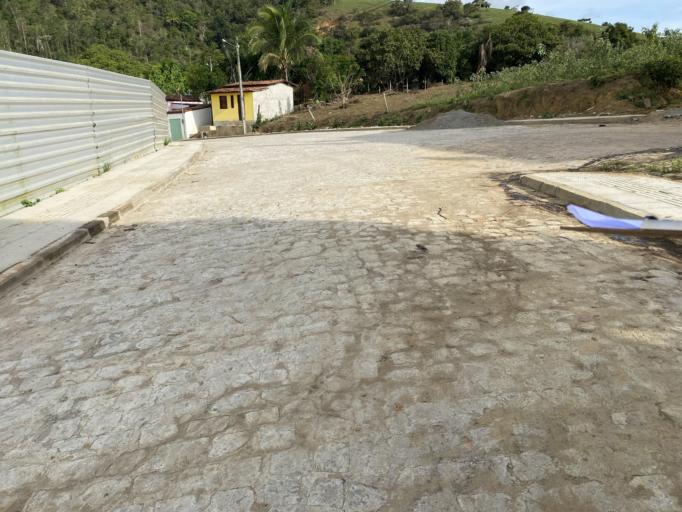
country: BR
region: Bahia
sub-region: Mutuipe
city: Mutuipe
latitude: -13.2580
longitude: -39.5643
